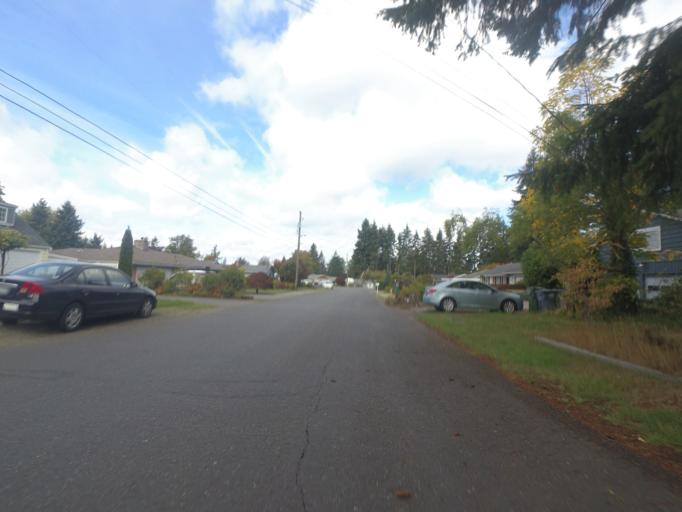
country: US
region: Washington
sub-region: Pierce County
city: University Place
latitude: 47.2176
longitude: -122.5438
